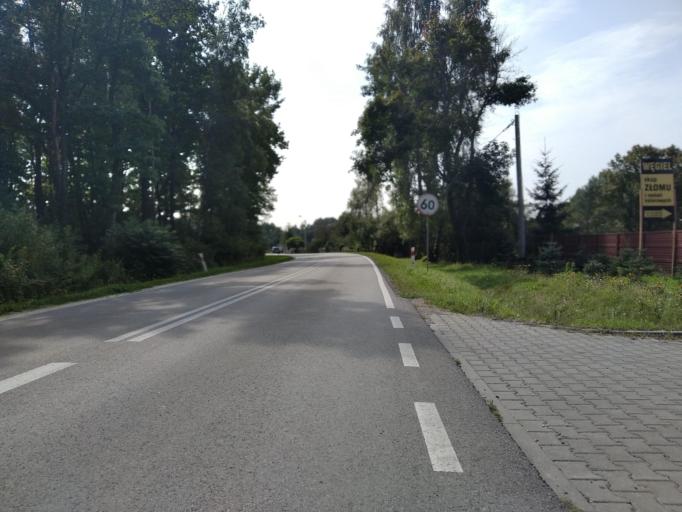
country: PL
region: Subcarpathian Voivodeship
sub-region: Powiat ropczycko-sedziszowski
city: Ostrow
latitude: 50.1211
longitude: 21.5853
